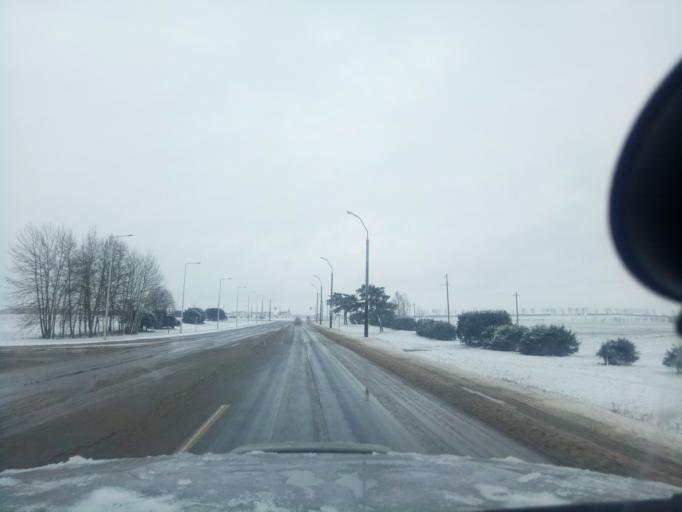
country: BY
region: Minsk
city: Nyasvizh
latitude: 53.2409
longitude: 26.6311
